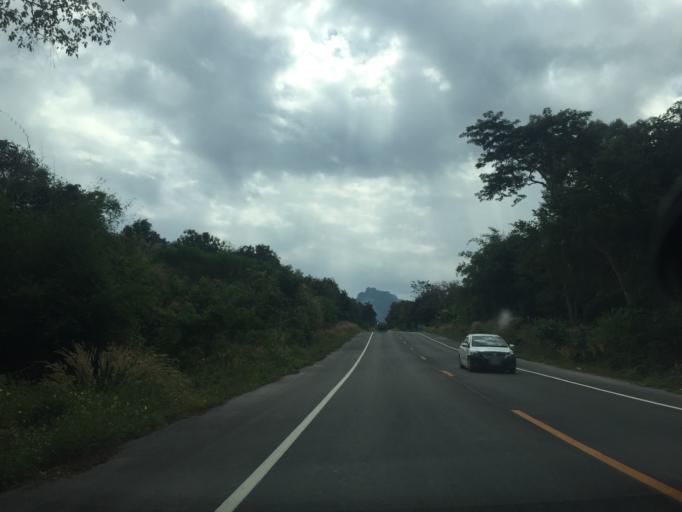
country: TH
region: Lampang
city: Mueang Pan
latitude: 18.8008
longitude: 99.5149
